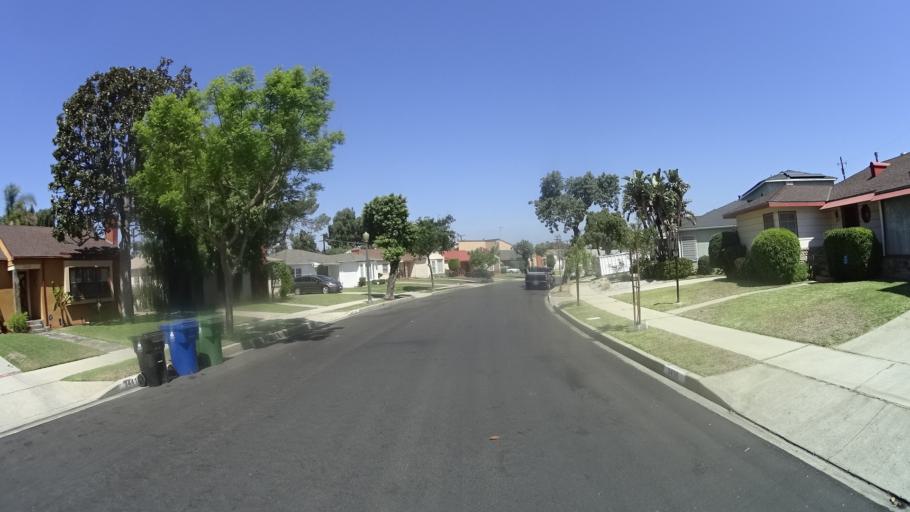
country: US
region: California
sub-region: Los Angeles County
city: View Park-Windsor Hills
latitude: 34.0242
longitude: -118.3621
